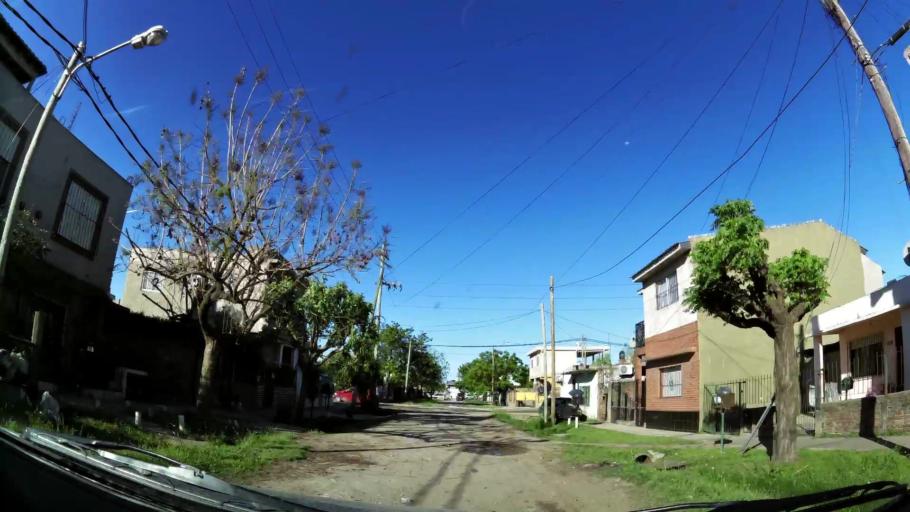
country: AR
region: Buenos Aires
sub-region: Partido de Quilmes
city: Quilmes
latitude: -34.7452
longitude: -58.3207
